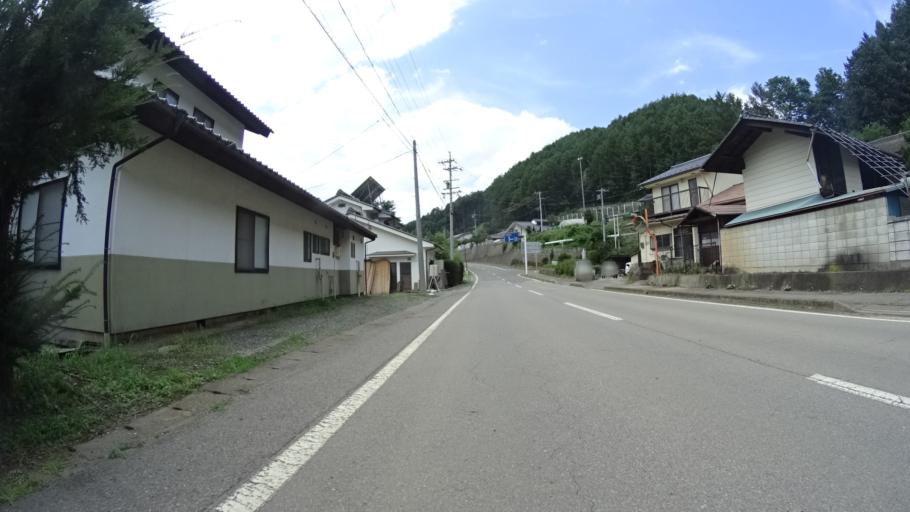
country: JP
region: Nagano
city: Saku
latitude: 36.0603
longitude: 138.5396
